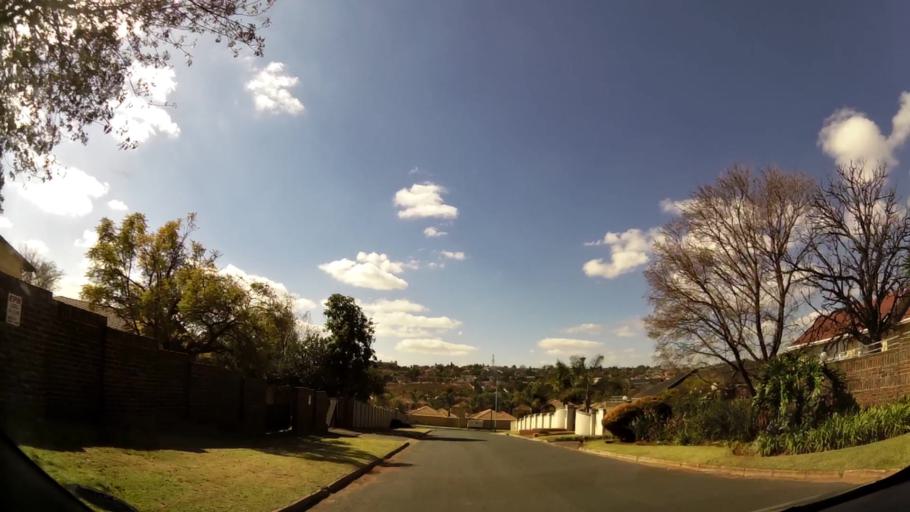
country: ZA
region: Gauteng
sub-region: West Rand District Municipality
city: Krugersdorp
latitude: -26.0952
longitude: 27.7979
